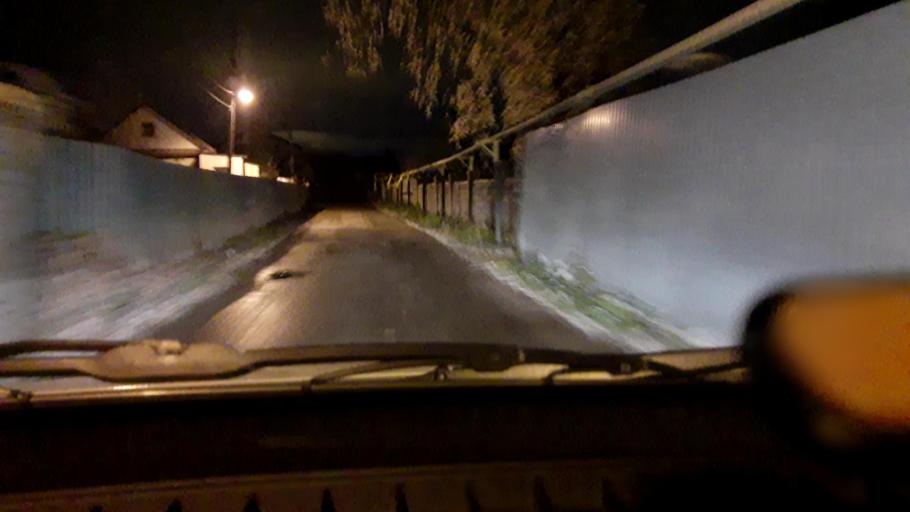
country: RU
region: Bashkortostan
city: Ufa
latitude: 54.6933
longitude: 55.9476
